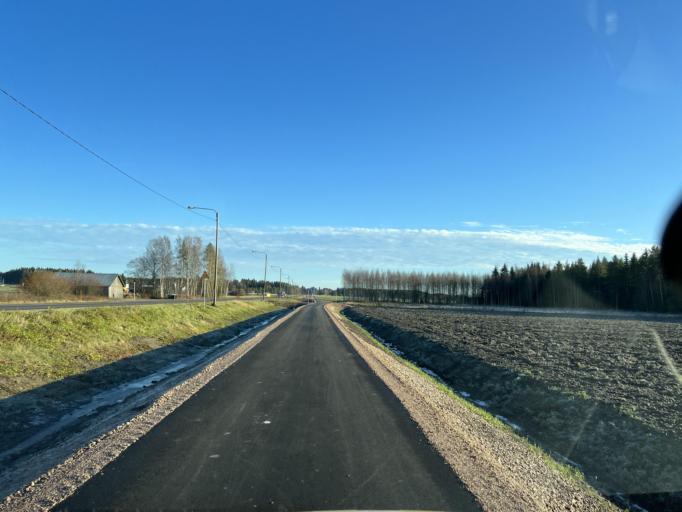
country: FI
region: Northern Ostrobothnia
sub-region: Nivala-Haapajaervi
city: Nivala
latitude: 63.9508
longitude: 24.8860
